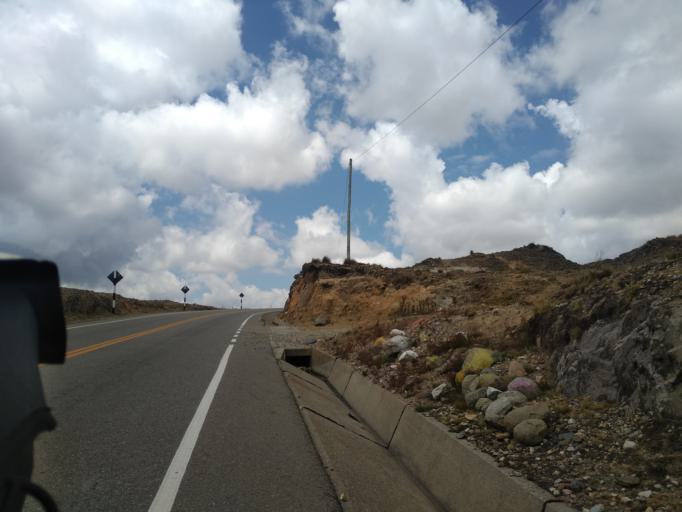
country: PE
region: La Libertad
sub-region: Provincia de Santiago de Chuco
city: Quiruvilca
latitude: -7.9508
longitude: -78.1917
